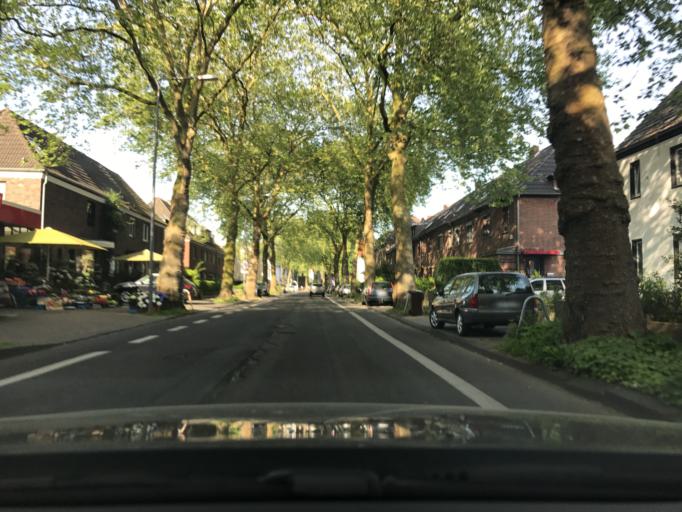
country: DE
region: North Rhine-Westphalia
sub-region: Regierungsbezirk Dusseldorf
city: Krefeld
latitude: 51.3446
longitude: 6.5929
